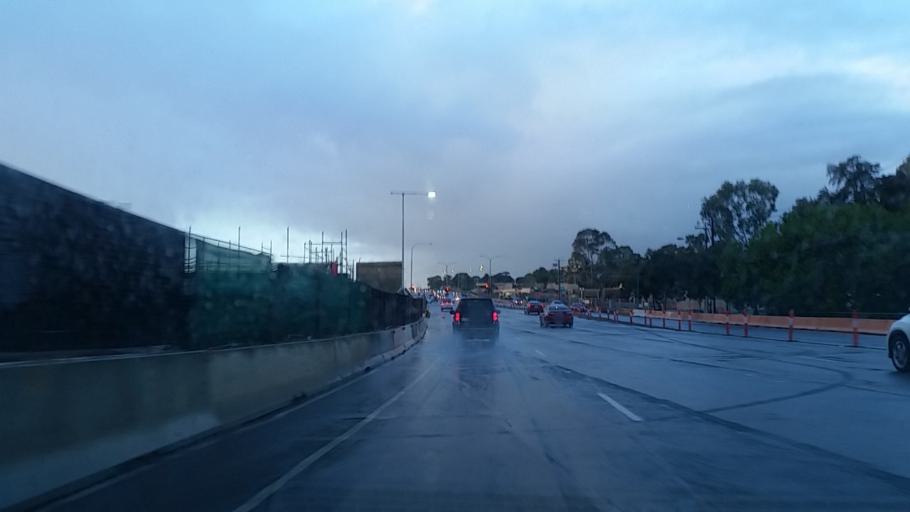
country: AU
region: South Australia
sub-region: Marion
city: Marion
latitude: -35.0236
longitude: 138.5625
